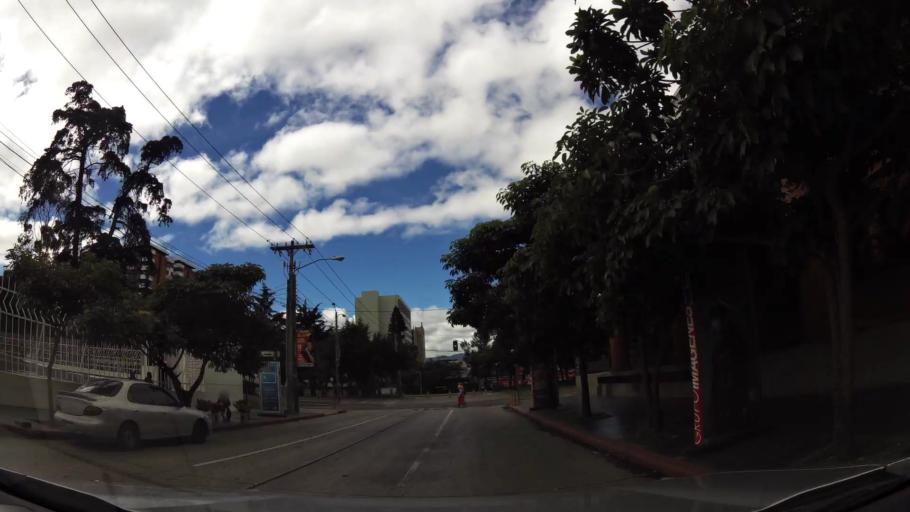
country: GT
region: Guatemala
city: Santa Catarina Pinula
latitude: 14.5971
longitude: -90.5167
